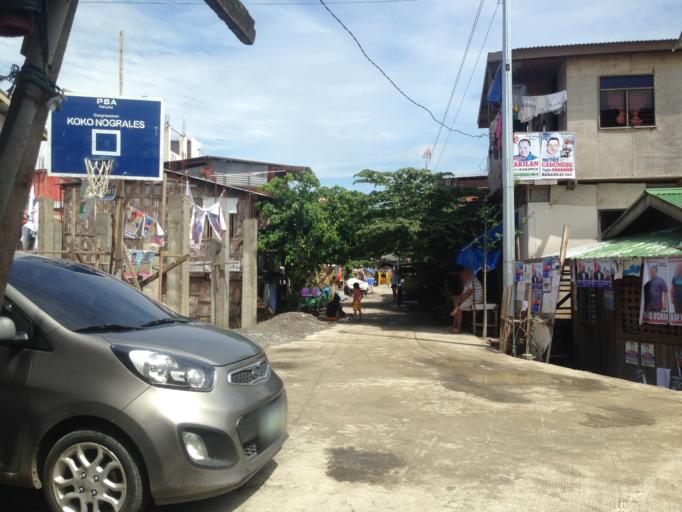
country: PH
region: Davao
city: Davao
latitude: 7.0690
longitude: 125.6223
